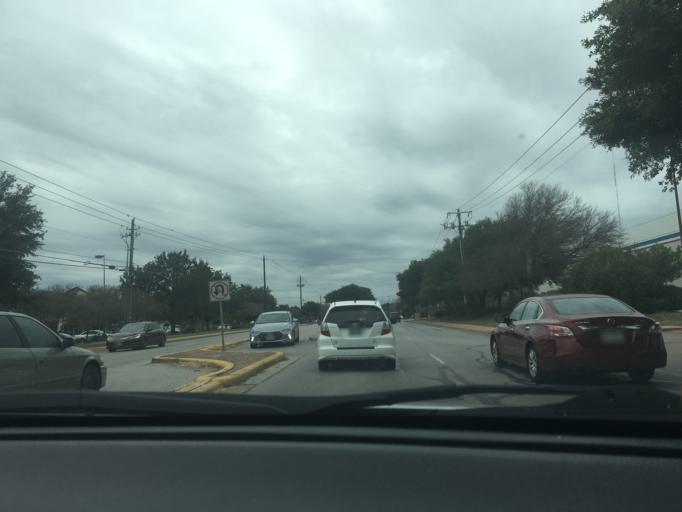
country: US
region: Texas
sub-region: Travis County
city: Rollingwood
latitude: 30.2279
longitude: -97.8215
